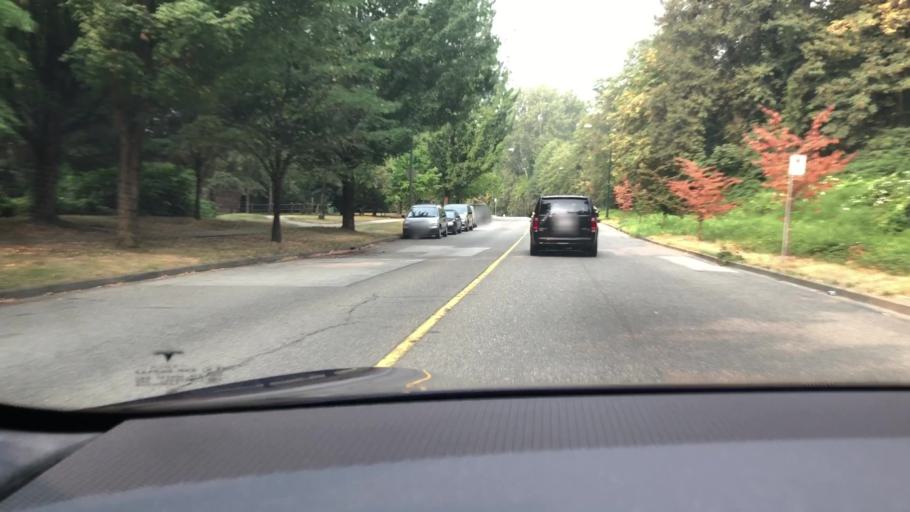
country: CA
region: British Columbia
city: Vancouver
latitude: 49.2084
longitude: -123.0357
